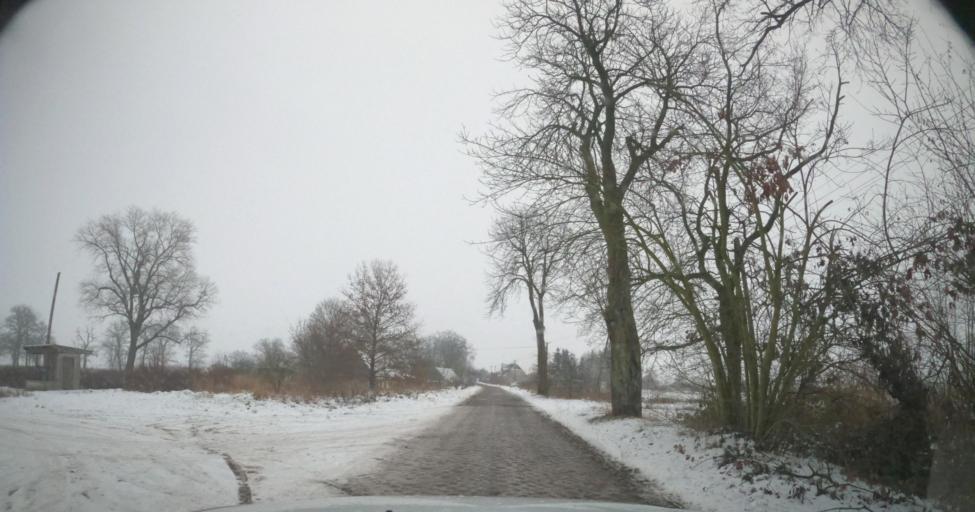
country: PL
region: West Pomeranian Voivodeship
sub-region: Powiat gryficki
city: Brojce
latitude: 53.9018
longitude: 15.3735
